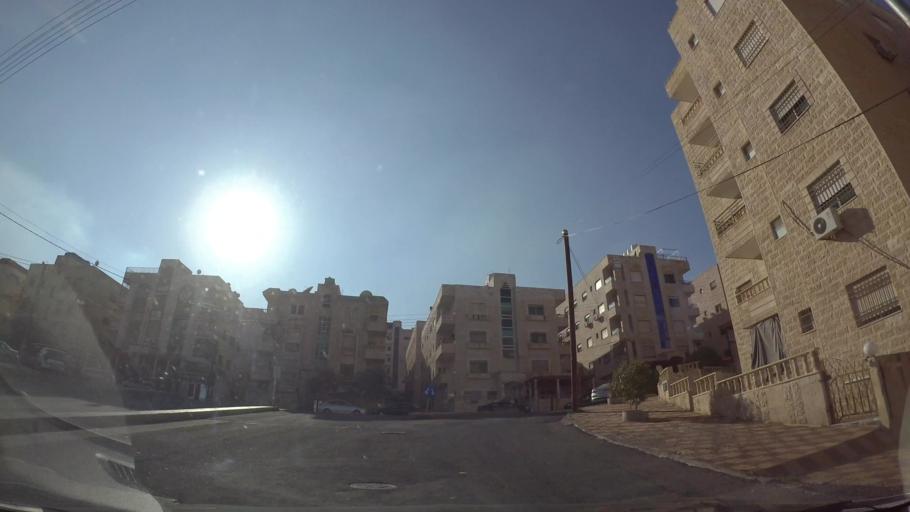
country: JO
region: Amman
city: Amman
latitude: 31.9830
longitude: 35.9432
